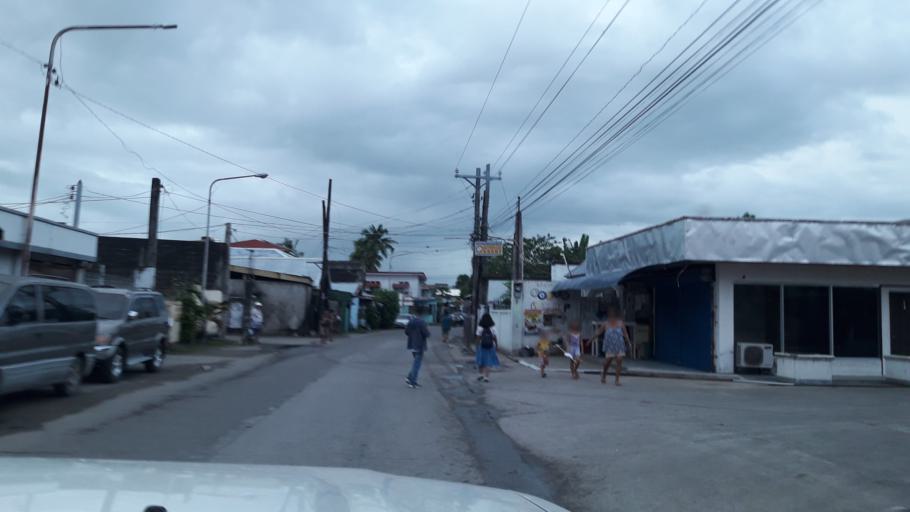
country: PH
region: Eastern Visayas
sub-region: Province of Leyte
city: Panalanoy
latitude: 11.2188
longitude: 125.0030
